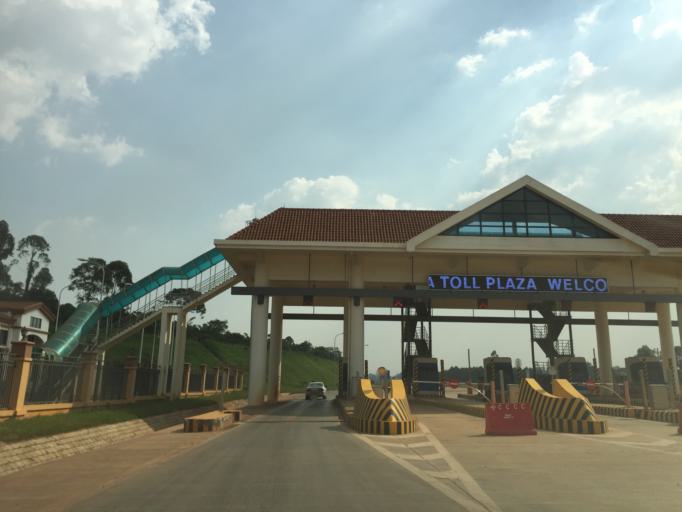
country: UG
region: Central Region
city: Kampala Central Division
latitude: 0.2967
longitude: 32.5127
